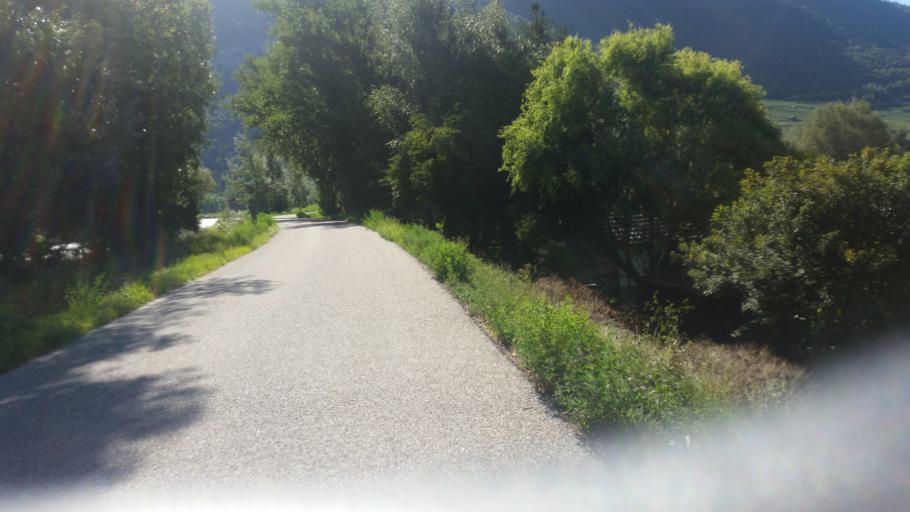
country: CH
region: Valais
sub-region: Sion District
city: Saint-Leonard
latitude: 46.2419
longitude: 7.4091
